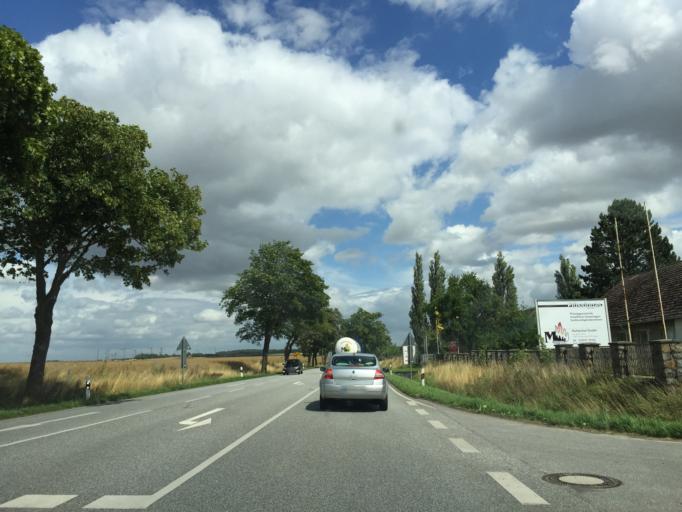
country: DE
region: Mecklenburg-Vorpommern
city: Rosenow
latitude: 53.6249
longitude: 13.0635
